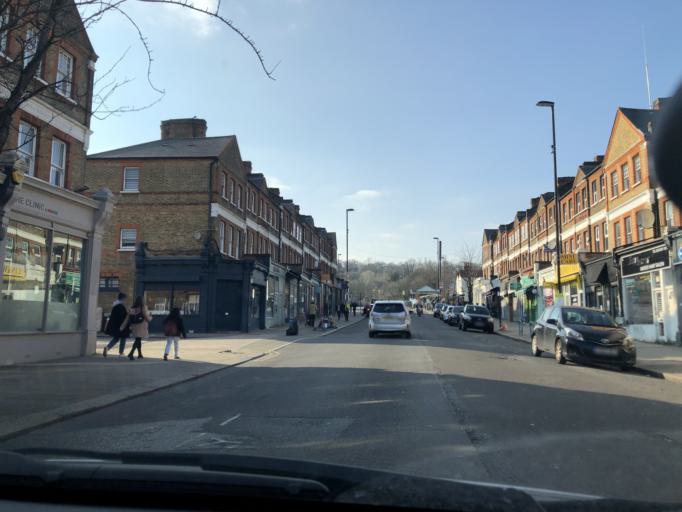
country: GB
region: England
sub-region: Greater London
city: Catford
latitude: 51.4493
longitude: -0.0435
